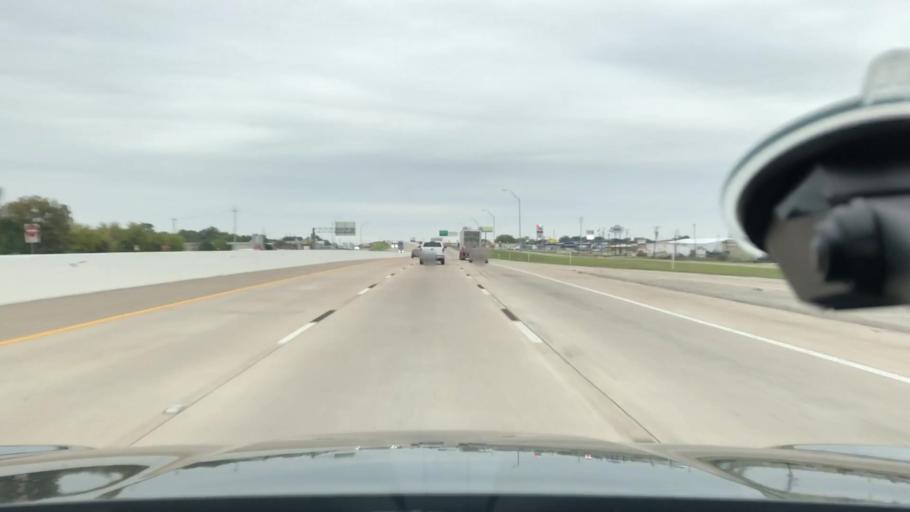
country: US
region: Texas
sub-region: McLennan County
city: Northcrest
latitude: 31.6636
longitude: -97.1001
